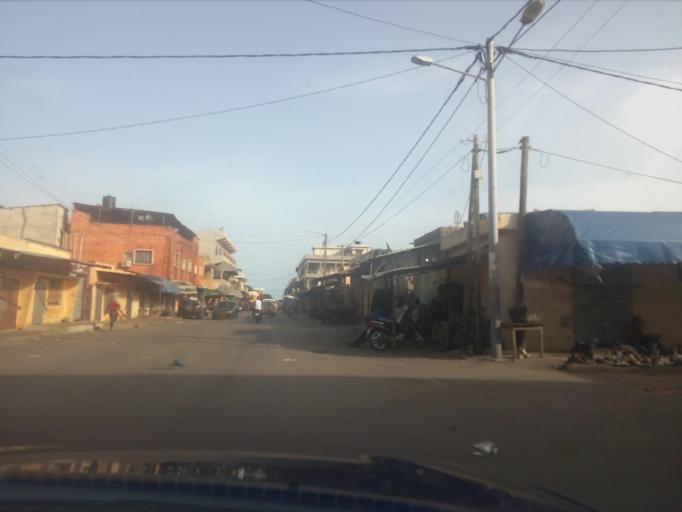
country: TG
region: Maritime
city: Lome
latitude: 6.1288
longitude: 1.2284
